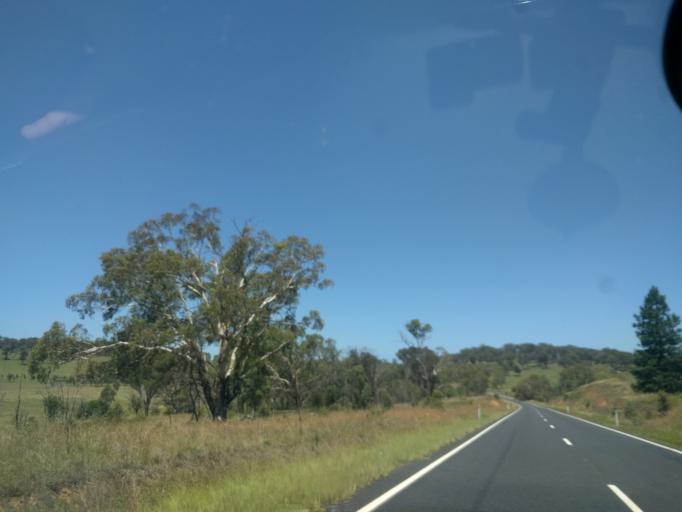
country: AU
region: New South Wales
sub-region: Armidale Dumaresq
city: Armidale
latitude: -30.5359
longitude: 151.7257
